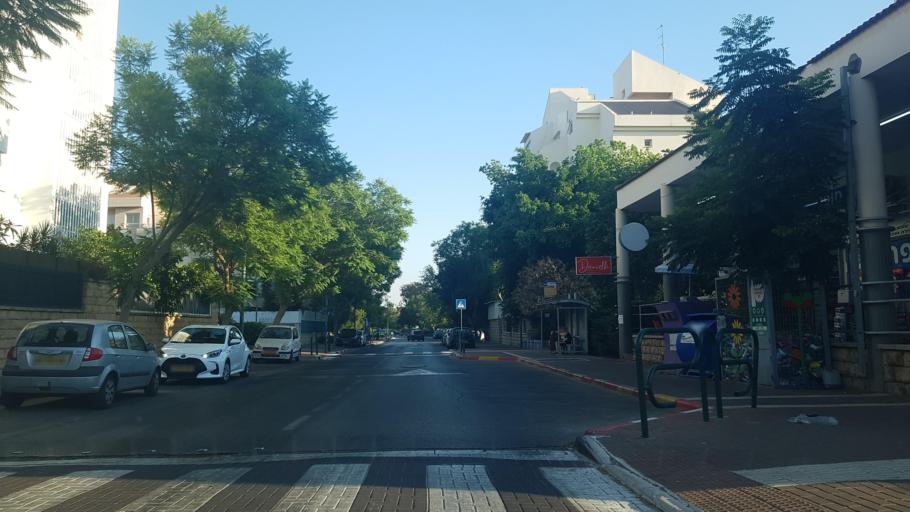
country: IL
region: Central District
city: Kfar Saba
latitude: 32.1796
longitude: 34.9351
